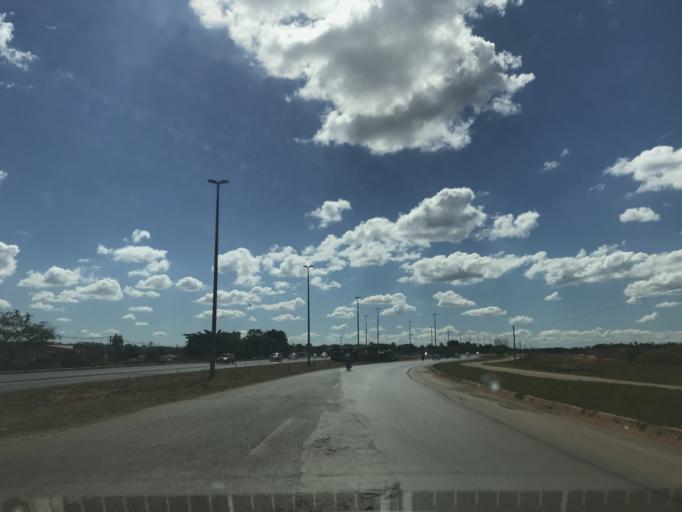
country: BR
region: Federal District
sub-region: Brasilia
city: Brasilia
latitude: -15.8014
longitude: -48.0010
